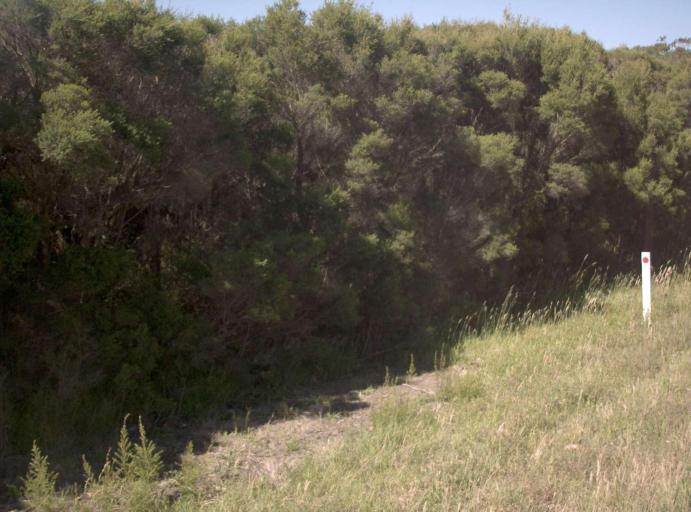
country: AU
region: Victoria
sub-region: Latrobe
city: Morwell
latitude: -38.6640
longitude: 146.4450
